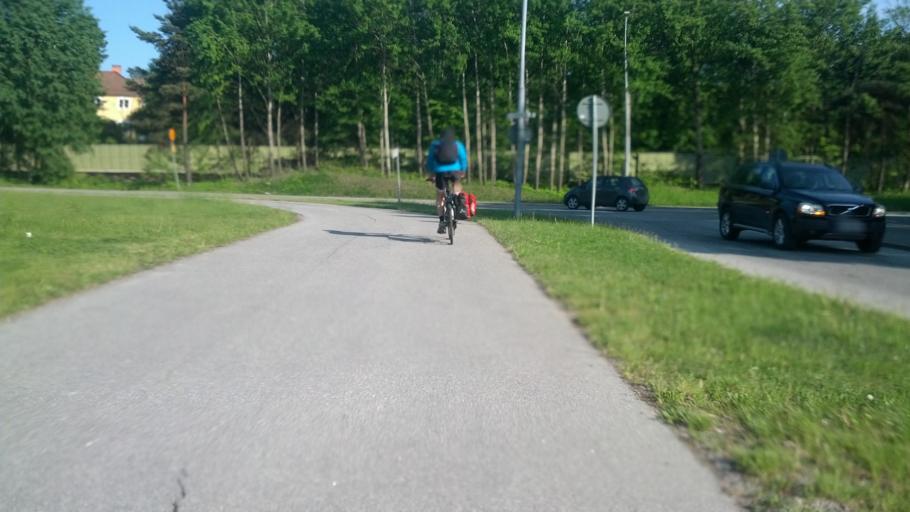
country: SE
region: Stockholm
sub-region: Danderyds Kommun
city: Djursholm
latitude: 59.3937
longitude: 18.0481
